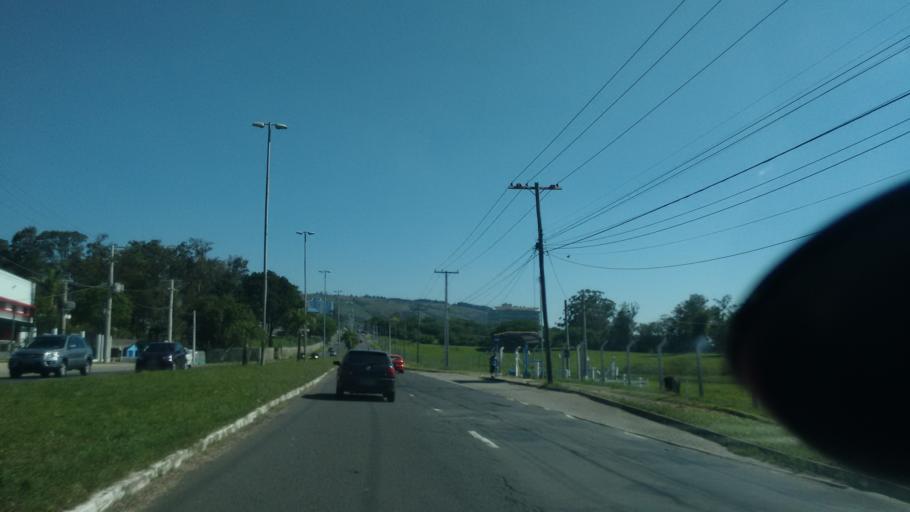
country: BR
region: Rio Grande do Sul
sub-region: Cachoeirinha
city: Cachoeirinha
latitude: -30.0268
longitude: -51.1202
